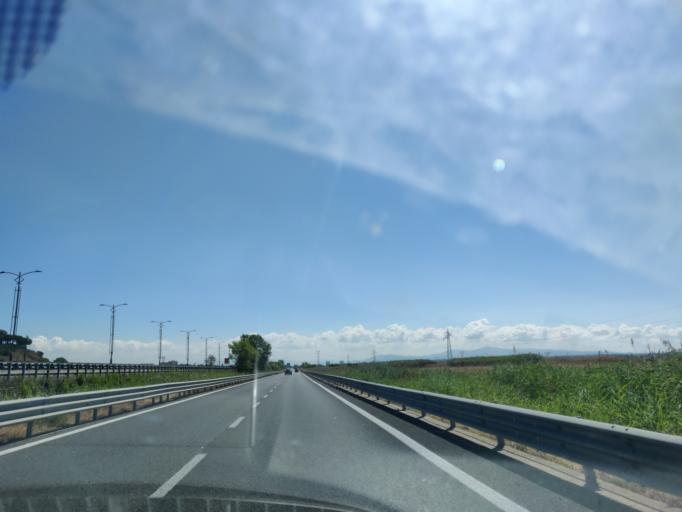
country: IT
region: Latium
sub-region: Citta metropolitana di Roma Capitale
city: Ponte Galeria-La Pisana
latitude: 41.8148
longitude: 12.3543
